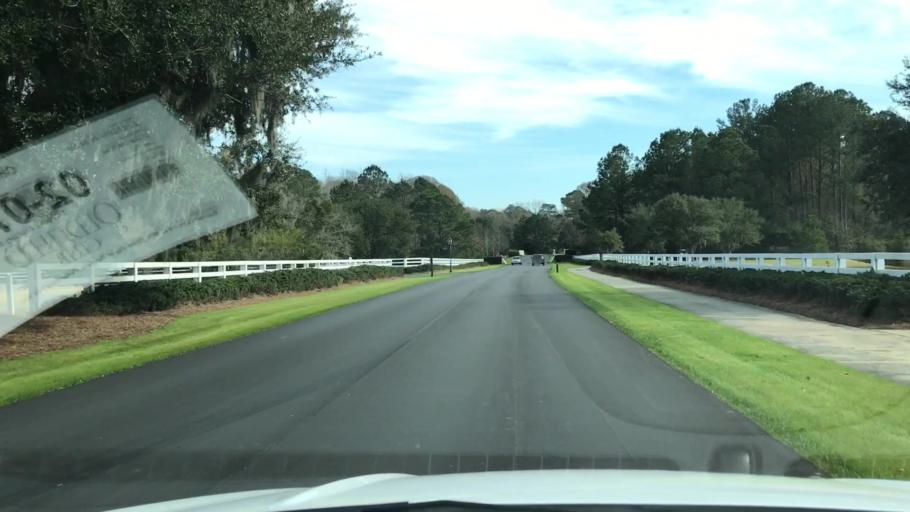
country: US
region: South Carolina
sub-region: Beaufort County
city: Bluffton
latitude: 32.3449
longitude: -80.9225
